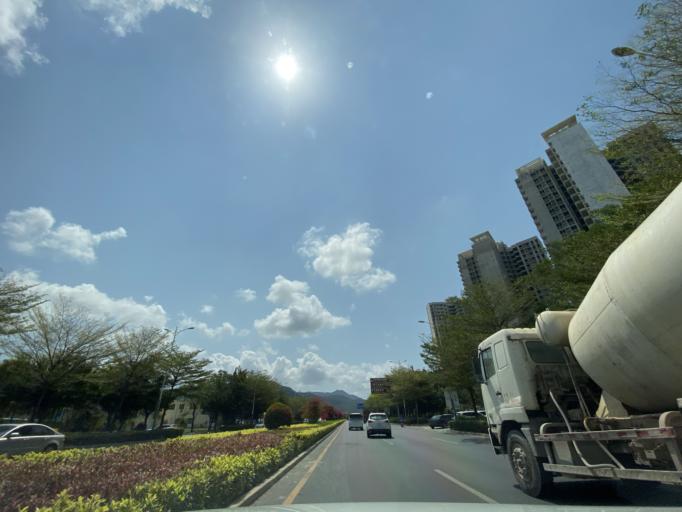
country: CN
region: Hainan
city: Tiandu
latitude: 18.2958
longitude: 109.5285
